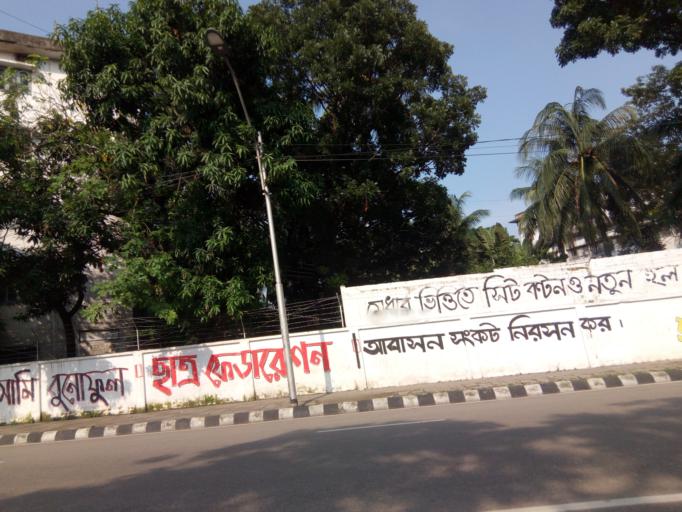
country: BD
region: Dhaka
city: Azimpur
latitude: 23.7285
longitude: 90.3953
